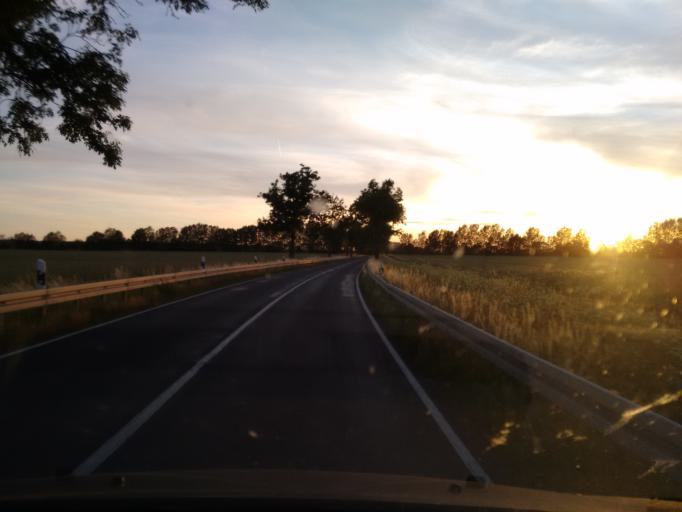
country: DE
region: Brandenburg
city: Beeskow
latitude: 52.1617
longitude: 14.2816
